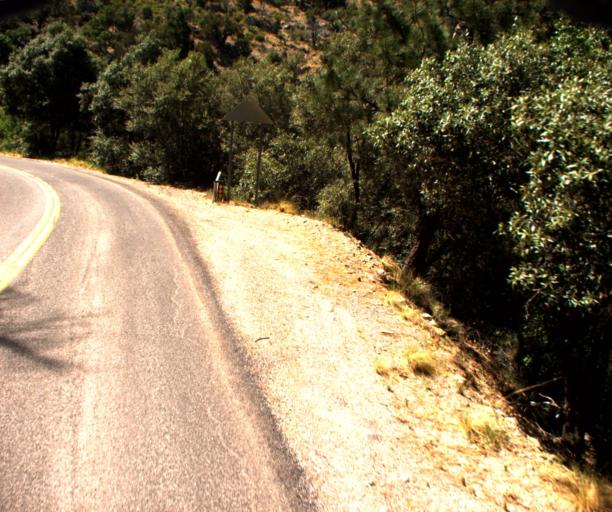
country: US
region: Arizona
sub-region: Graham County
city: Swift Trail Junction
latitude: 32.6511
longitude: -109.8116
